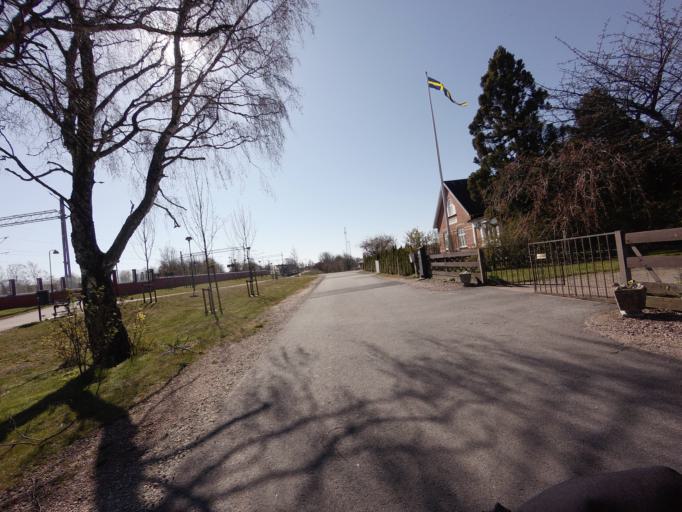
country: SE
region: Skane
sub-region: Malmo
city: Oxie
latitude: 55.4686
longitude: 13.1317
